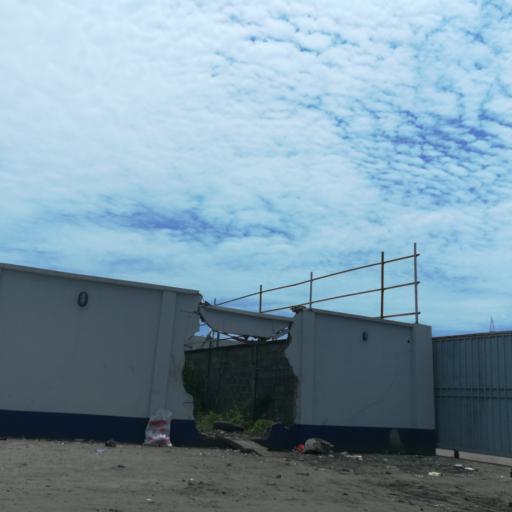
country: NG
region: Lagos
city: Ebute Metta
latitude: 6.4683
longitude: 3.3818
